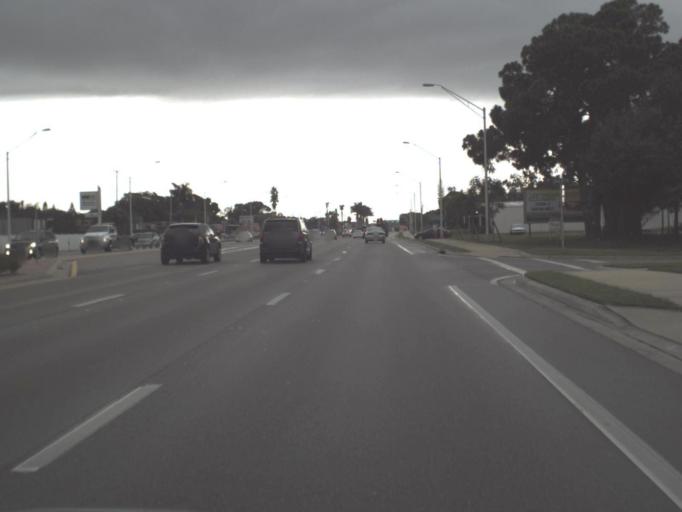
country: US
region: Florida
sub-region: Sarasota County
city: North Sarasota
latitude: 27.3652
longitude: -82.5308
